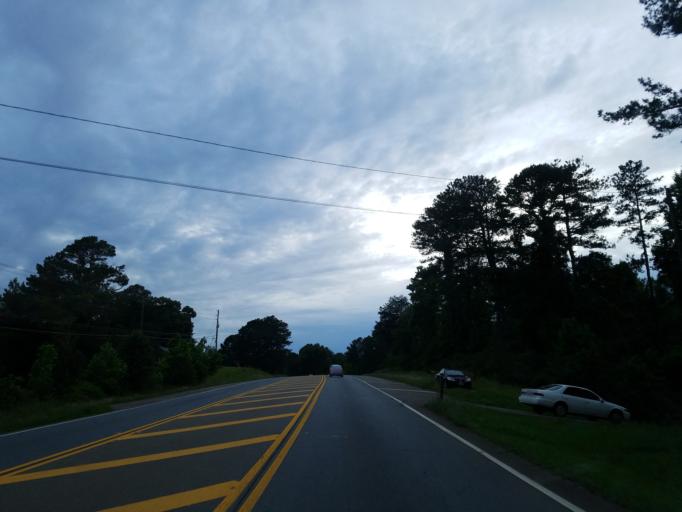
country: US
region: Georgia
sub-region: Cherokee County
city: Ball Ground
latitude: 34.2575
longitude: -84.3235
